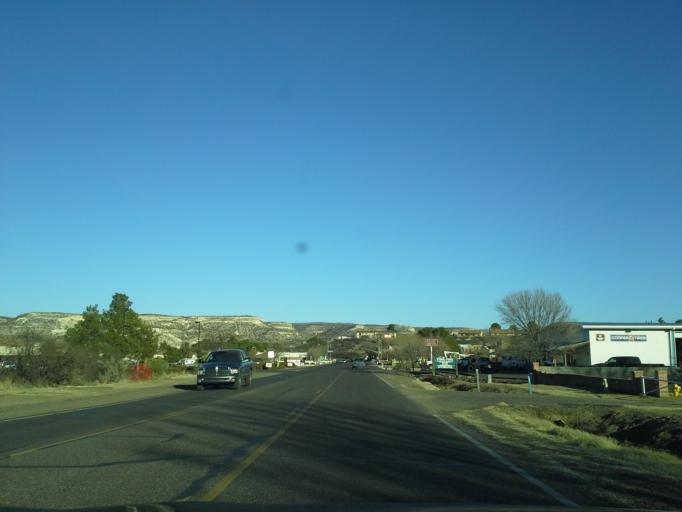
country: US
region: Arizona
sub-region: Yavapai County
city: Camp Verde
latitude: 34.5657
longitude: -111.8664
